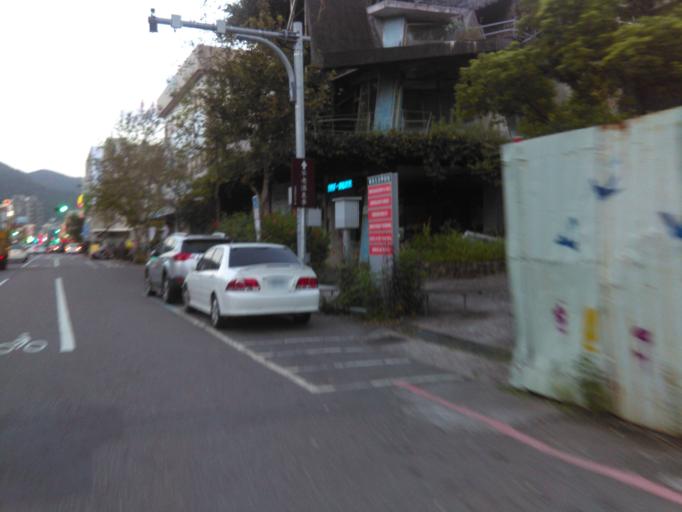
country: TW
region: Taiwan
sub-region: Yilan
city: Yilan
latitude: 24.8207
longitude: 121.7695
